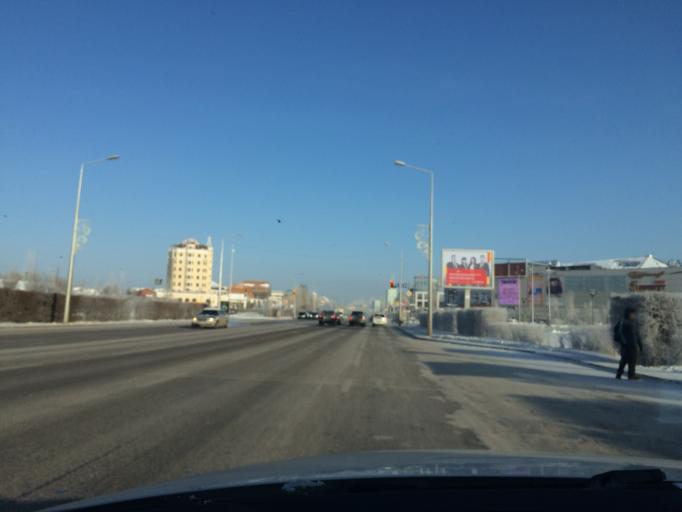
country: KZ
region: Astana Qalasy
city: Astana
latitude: 51.1362
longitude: 71.4084
